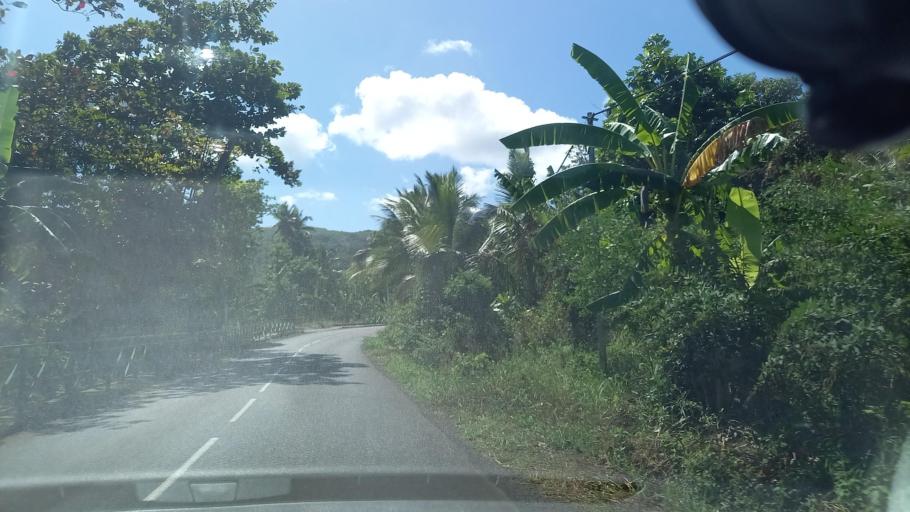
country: YT
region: Kani-Keli
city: Kani Keli
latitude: -12.9577
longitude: 45.1133
